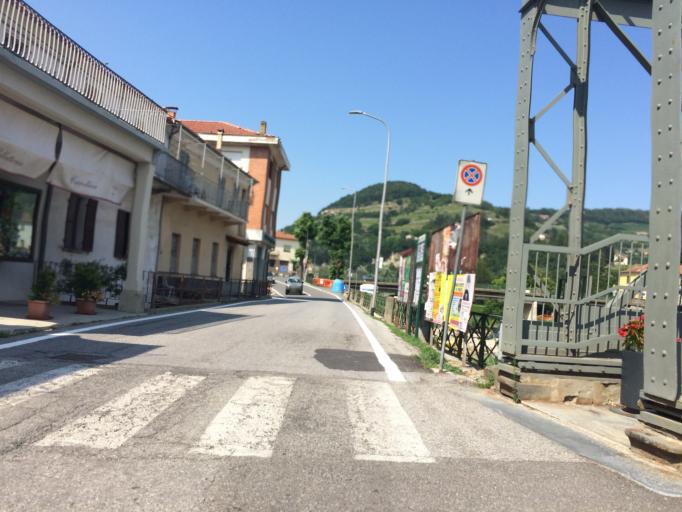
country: IT
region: Piedmont
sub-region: Provincia di Cuneo
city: Cortemilia
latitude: 44.5797
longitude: 8.1918
